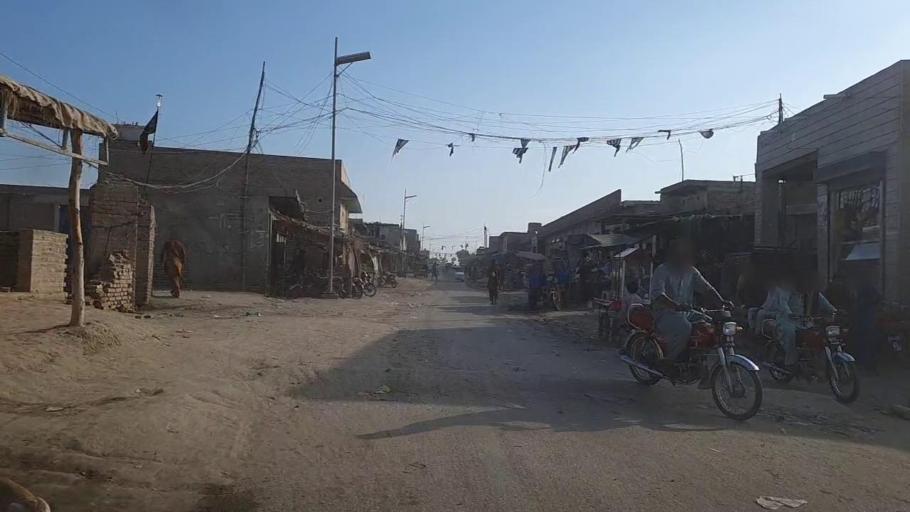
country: PK
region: Sindh
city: Thul
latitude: 28.1821
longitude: 68.7259
